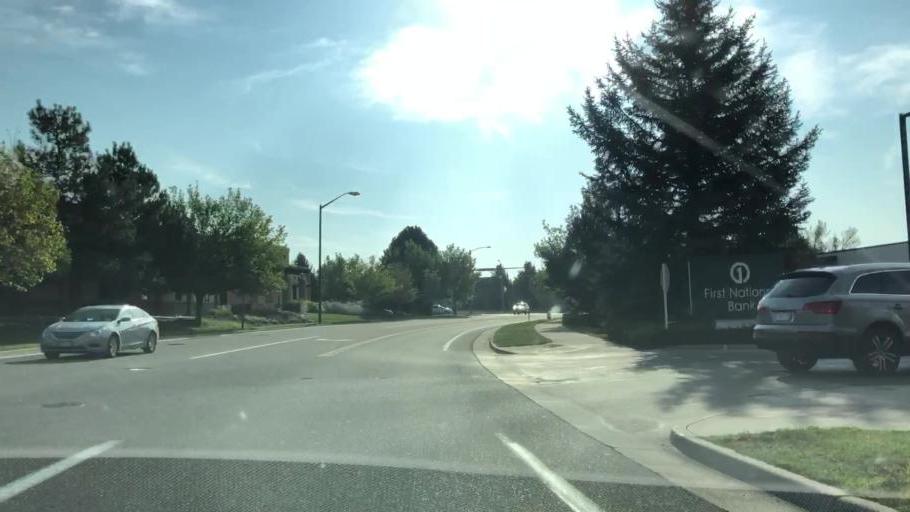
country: US
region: Colorado
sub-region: Larimer County
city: Fort Collins
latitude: 40.5325
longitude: -105.0759
